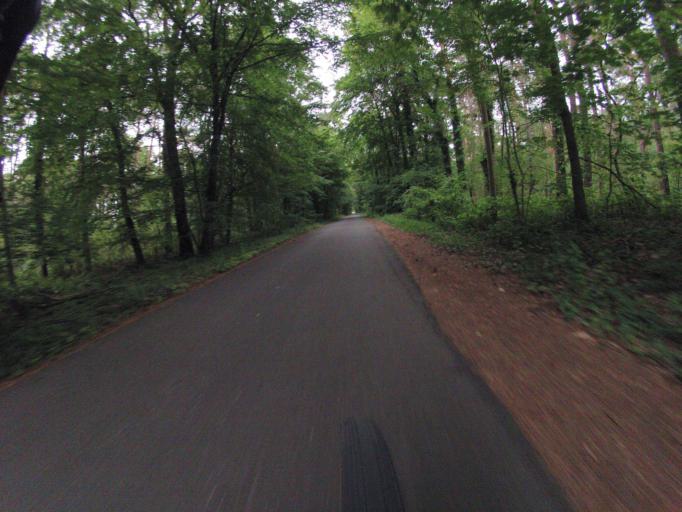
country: DE
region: North Rhine-Westphalia
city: Emsdetten
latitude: 52.1991
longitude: 7.5500
